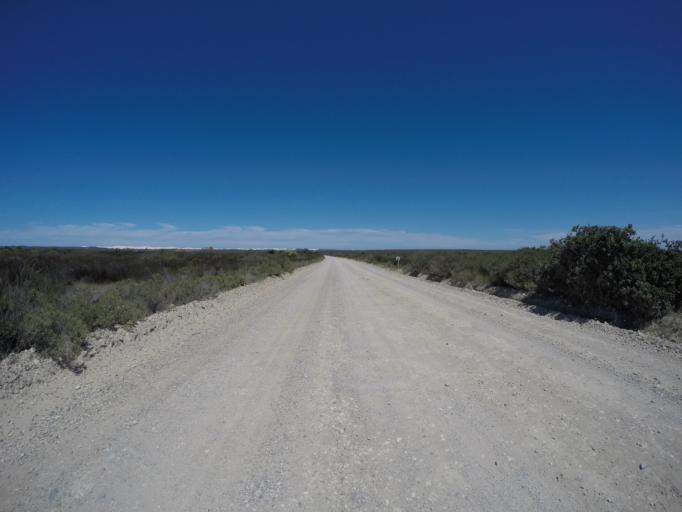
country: ZA
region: Western Cape
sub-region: Overberg District Municipality
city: Bredasdorp
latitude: -34.4460
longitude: 20.4221
